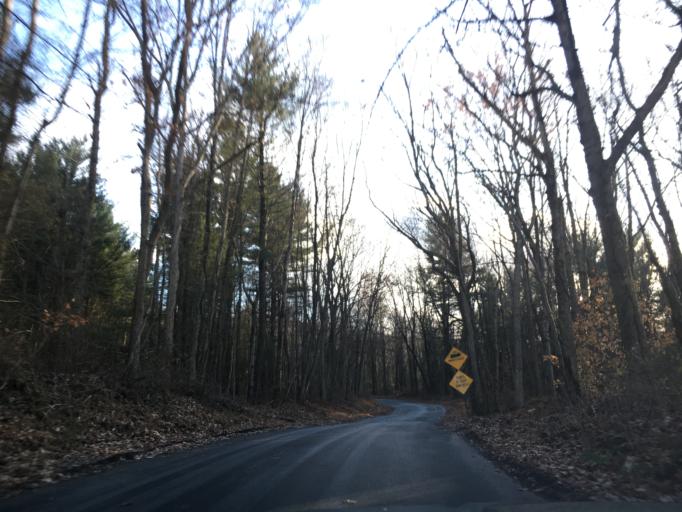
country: US
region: Pennsylvania
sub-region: Carbon County
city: Lehighton
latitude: 40.7733
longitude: -75.7104
